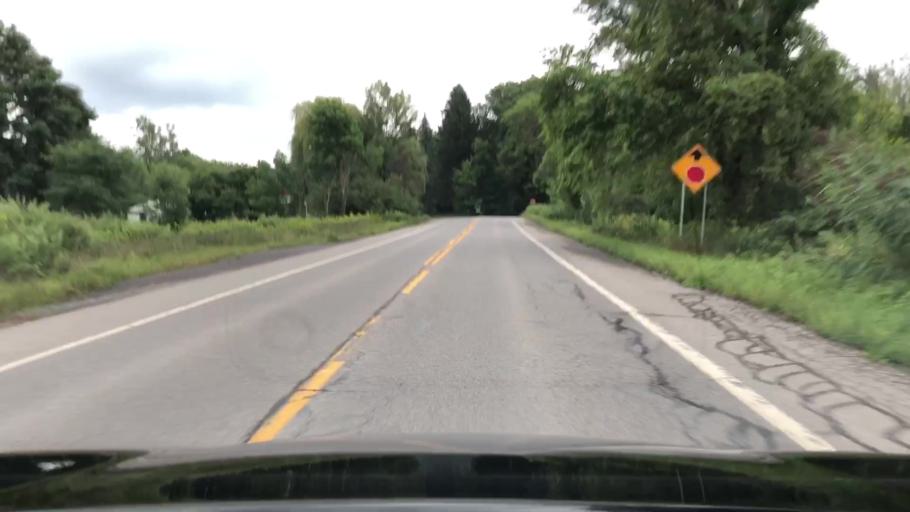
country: US
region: New York
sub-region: Erie County
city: Orchard Park
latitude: 42.7544
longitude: -78.6969
